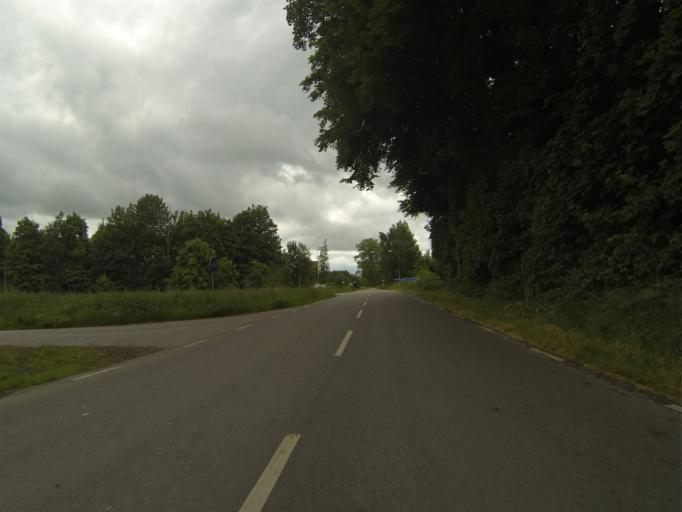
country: SE
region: Skane
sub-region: Lunds Kommun
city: Veberod
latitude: 55.6827
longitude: 13.4241
